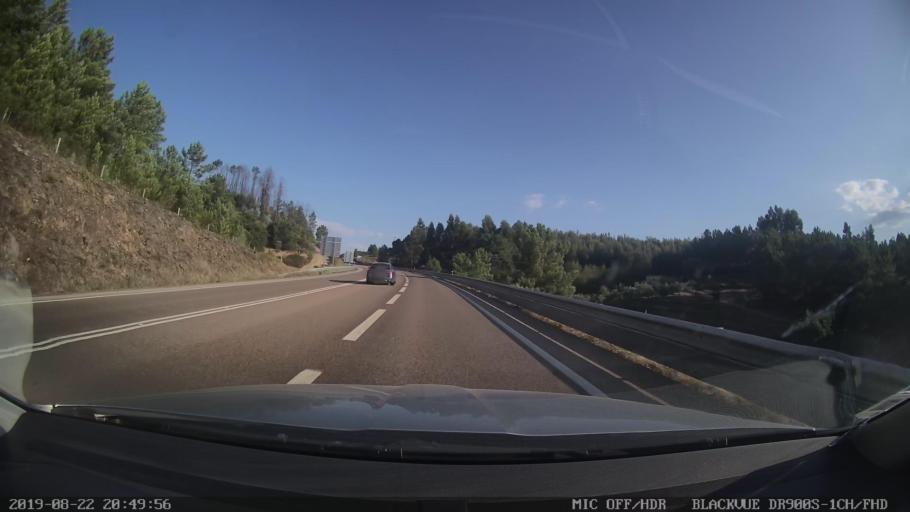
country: PT
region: Castelo Branco
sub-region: Proenca-A-Nova
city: Proenca-a-Nova
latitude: 39.7487
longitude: -7.9342
